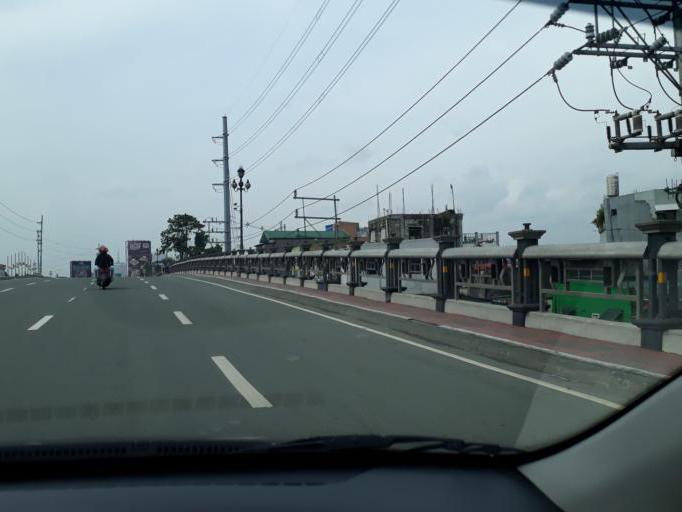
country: PH
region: Metro Manila
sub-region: City of Manila
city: Quiapo
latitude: 14.5943
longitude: 121.0016
